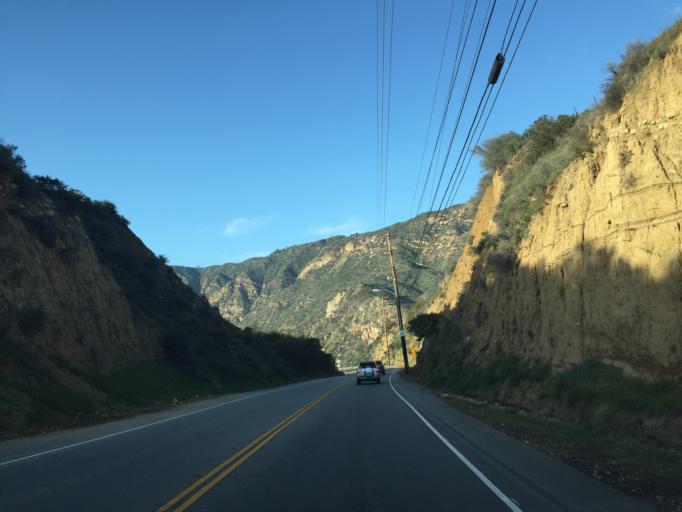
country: US
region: California
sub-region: Los Angeles County
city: Malibu Beach
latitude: 34.0447
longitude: -118.6924
